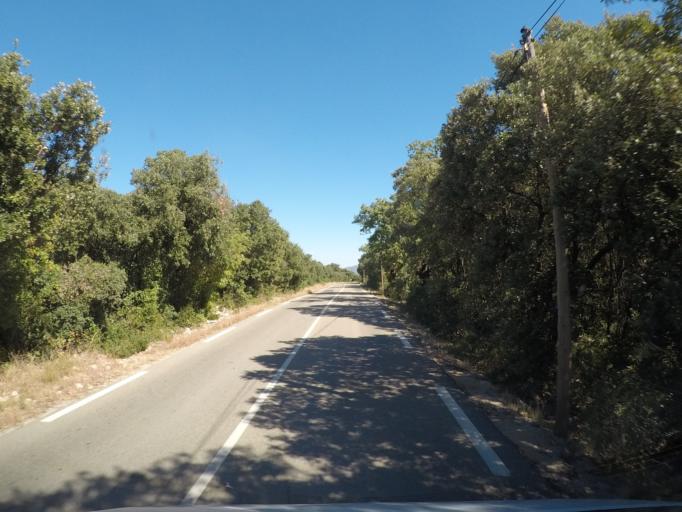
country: FR
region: Languedoc-Roussillon
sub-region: Departement de l'Herault
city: Vailhauques
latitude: 43.7308
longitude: 3.6810
